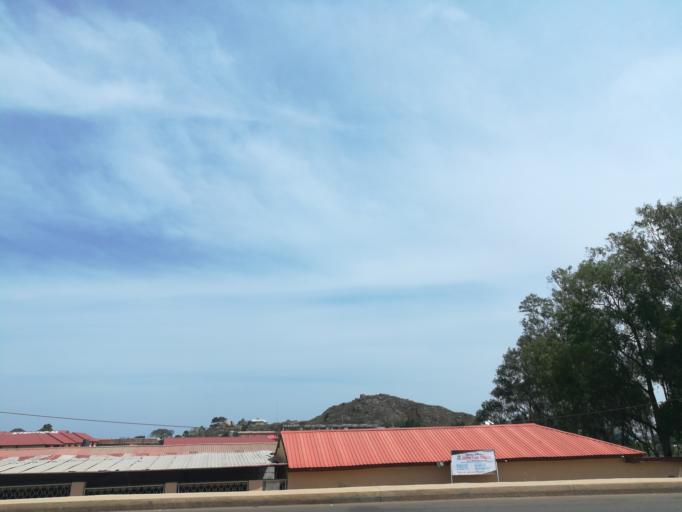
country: NG
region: Plateau
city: Bukuru
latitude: 9.8443
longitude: 8.8664
